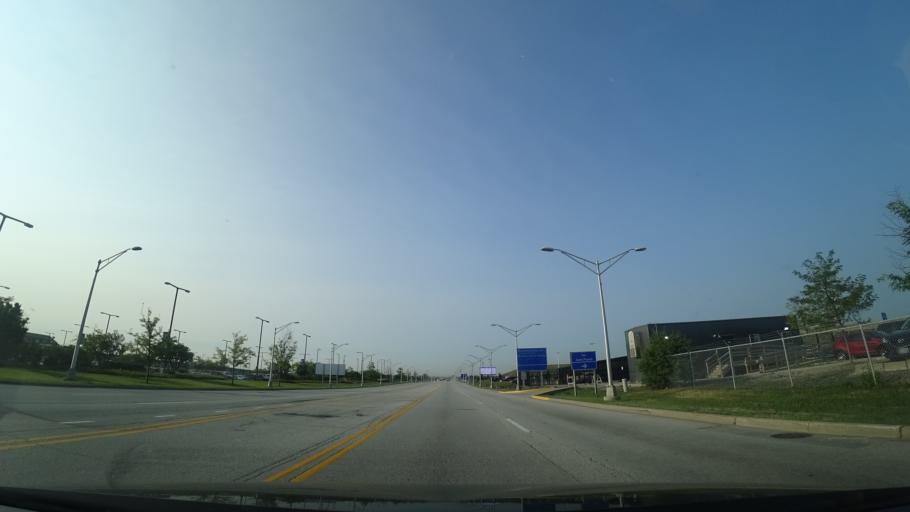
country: US
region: Illinois
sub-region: Cook County
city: Rosemont
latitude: 41.9897
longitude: -87.8858
